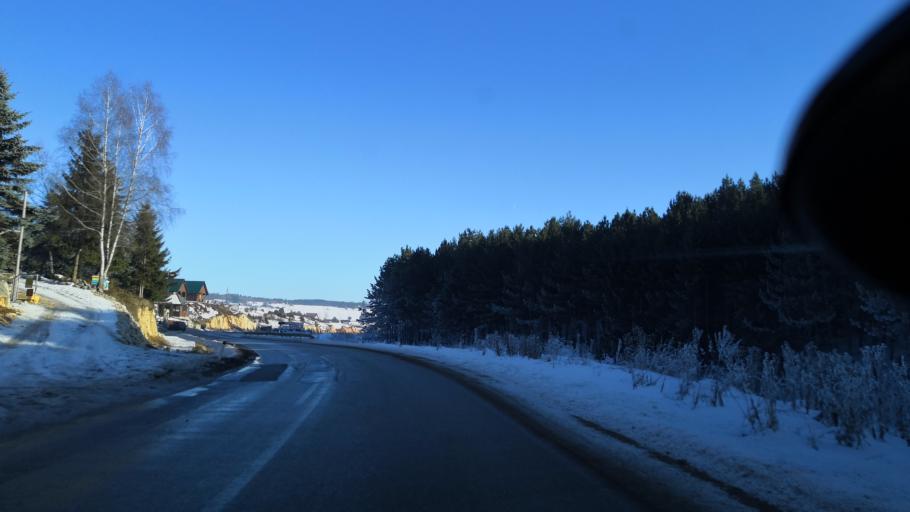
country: BA
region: Republika Srpska
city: Sokolac
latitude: 43.9360
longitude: 18.8142
